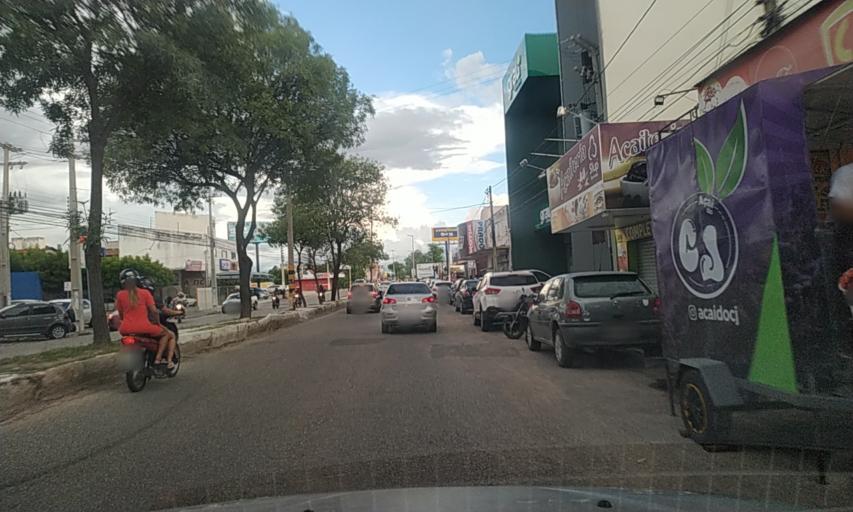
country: BR
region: Rio Grande do Norte
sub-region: Mossoro
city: Mossoro
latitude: -5.2022
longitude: -37.3381
